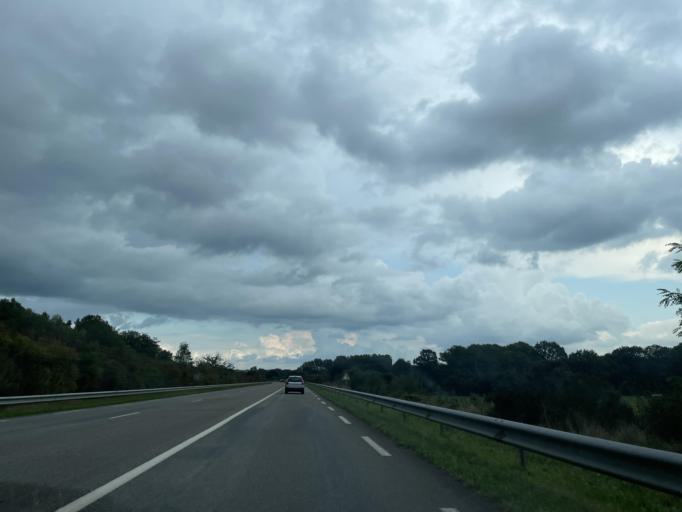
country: FR
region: Haute-Normandie
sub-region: Departement de la Seine-Maritime
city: Forges-les-Eaux
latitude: 49.6010
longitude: 1.5557
